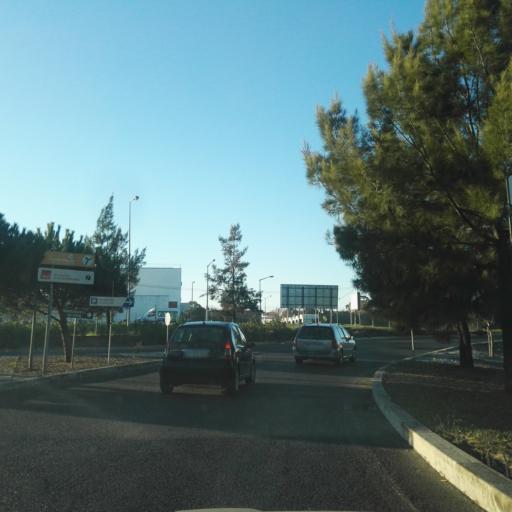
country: PT
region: Lisbon
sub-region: Loures
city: Sacavem
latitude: 38.7817
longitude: -9.1241
